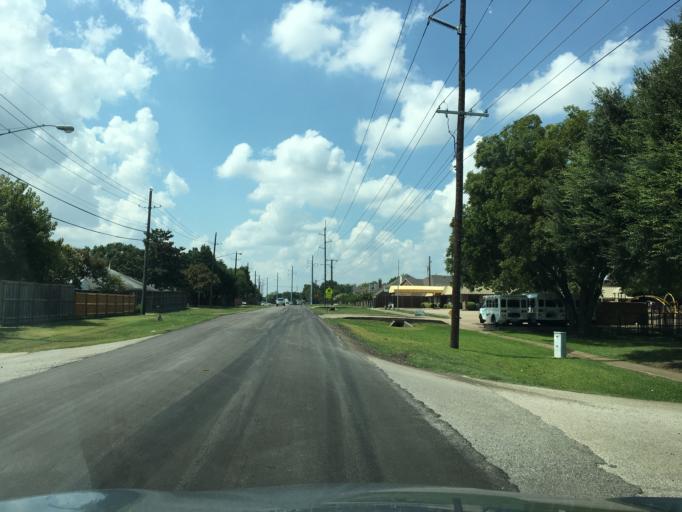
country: US
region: Texas
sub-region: Dallas County
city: Garland
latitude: 32.9498
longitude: -96.6397
